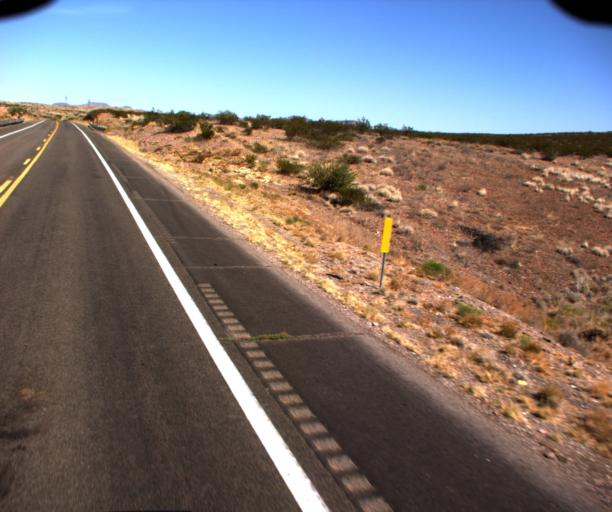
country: US
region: Arizona
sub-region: Greenlee County
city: Clifton
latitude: 32.7380
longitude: -109.2006
